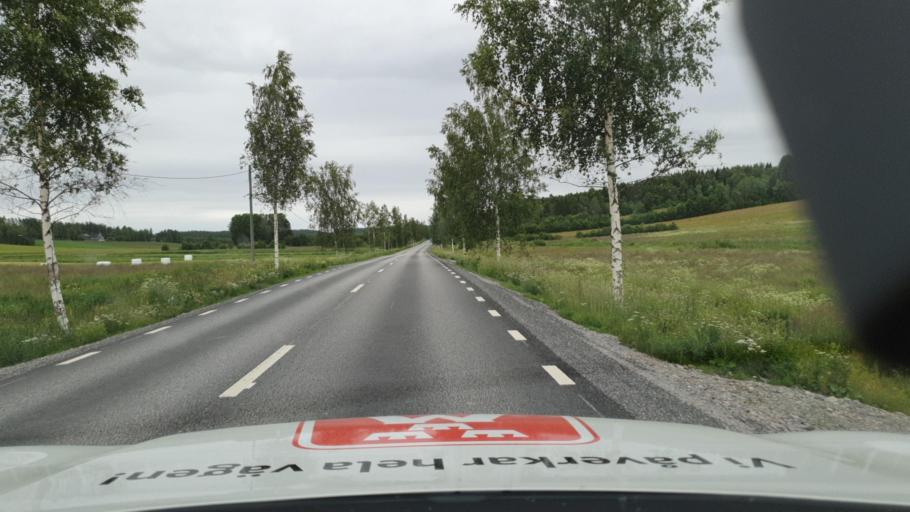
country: SE
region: Vaesterbotten
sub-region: Vannas Kommun
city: Vaennaes
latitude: 63.7545
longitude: 19.6375
